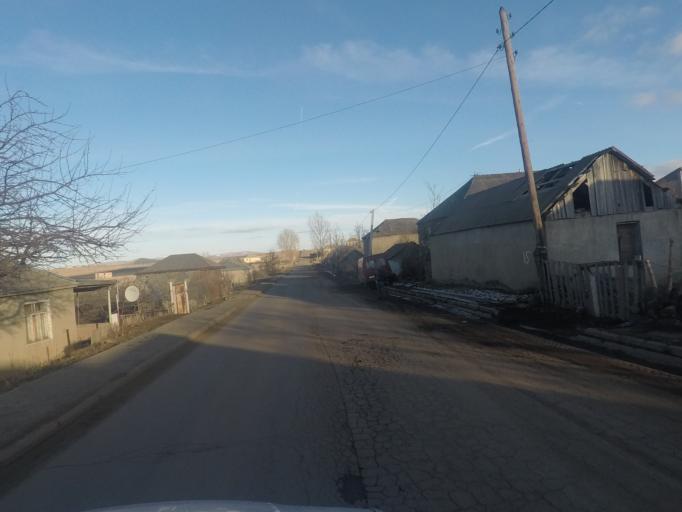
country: GE
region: Kvemo Kartli
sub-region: Tsalka
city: Tsalka
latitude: 41.5991
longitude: 44.0129
